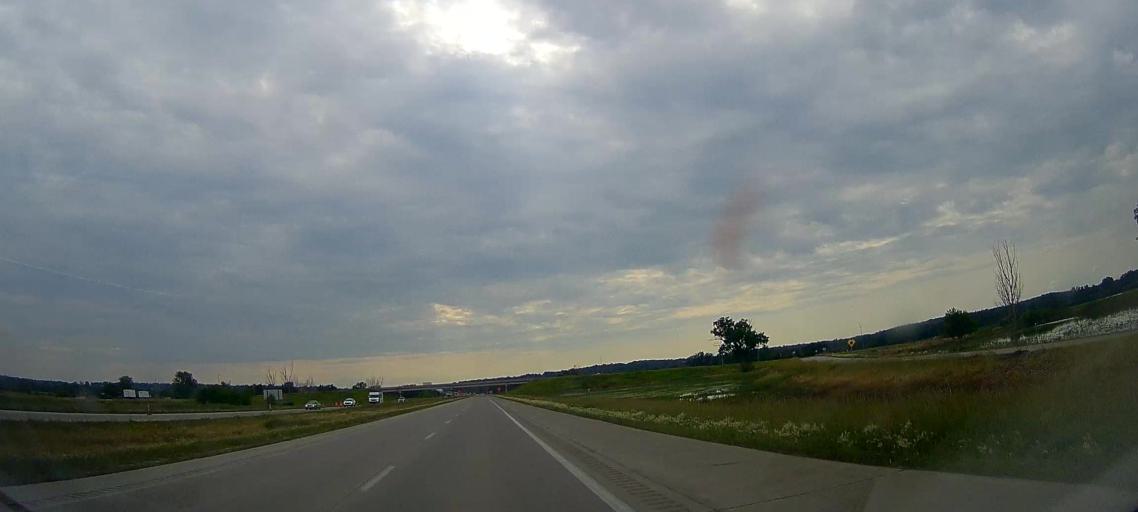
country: US
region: Iowa
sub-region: Pottawattamie County
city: Carter Lake
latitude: 41.3466
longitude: -95.9320
